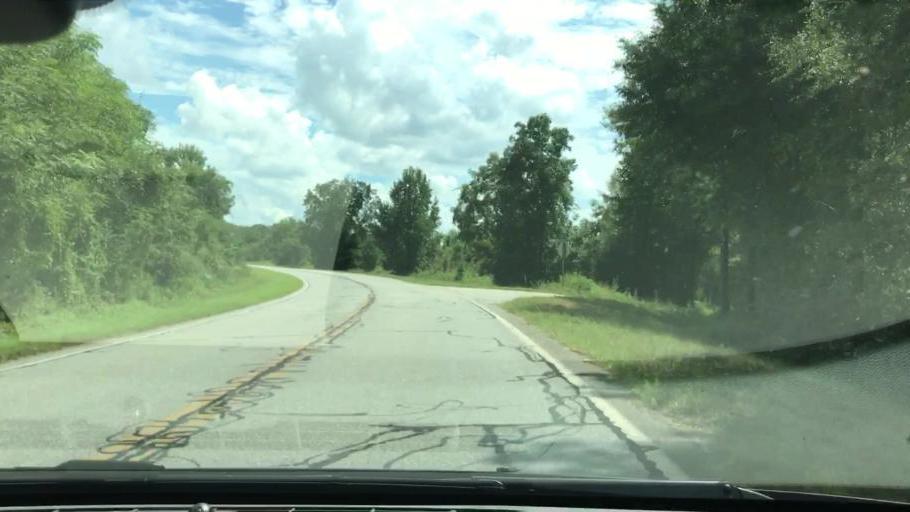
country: US
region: Georgia
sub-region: Quitman County
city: Georgetown
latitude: 32.0452
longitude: -85.0363
